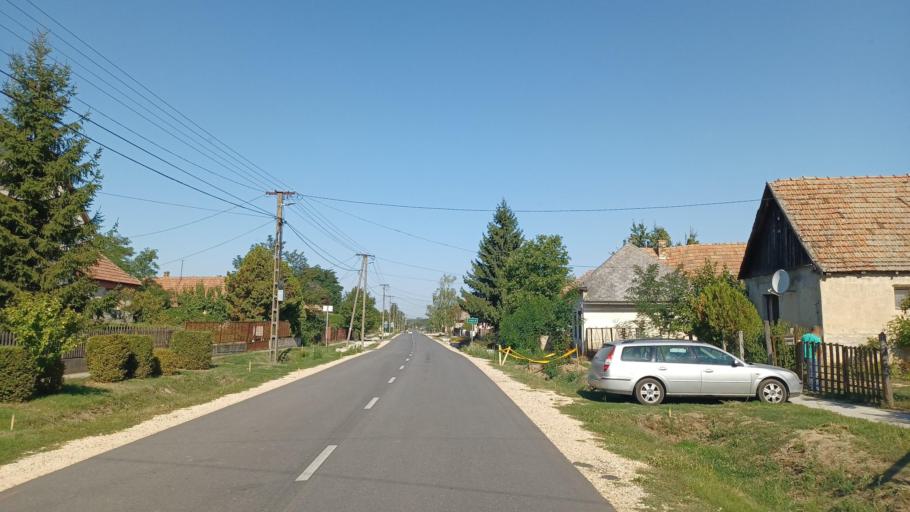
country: HU
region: Tolna
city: Nemetker
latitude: 46.7263
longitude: 18.7532
